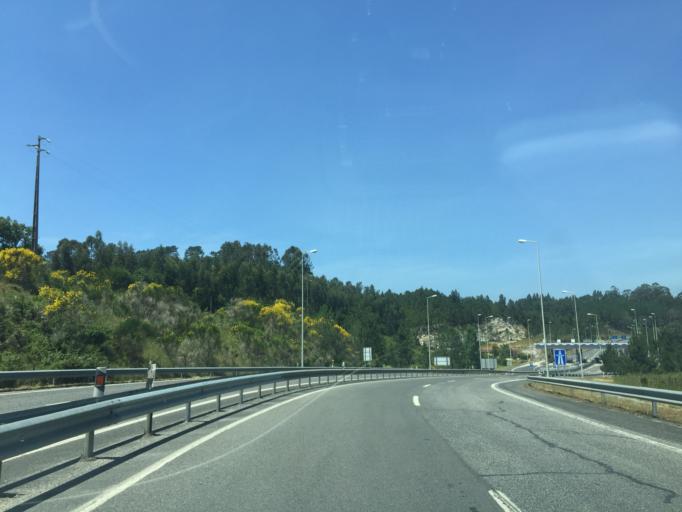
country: PT
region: Lisbon
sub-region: Mafra
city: Venda do Pinheiro
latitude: 38.9022
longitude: -9.2047
